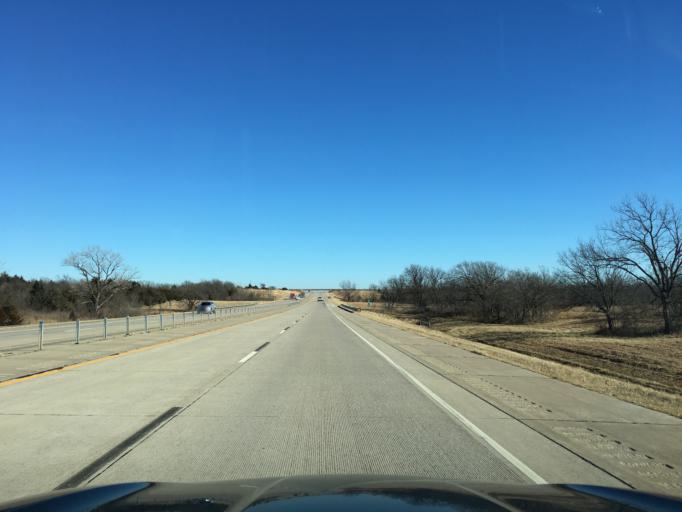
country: US
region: Oklahoma
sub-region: Payne County
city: Yale
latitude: 36.2249
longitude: -96.7071
